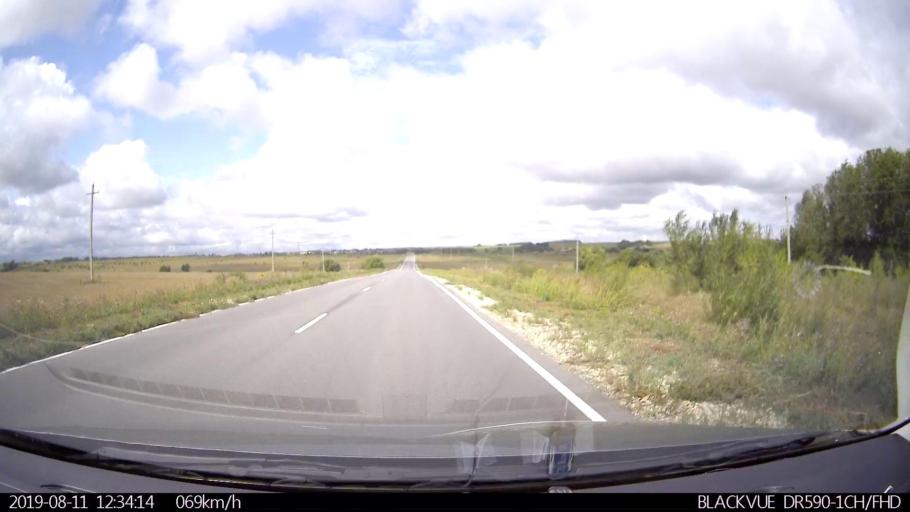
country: RU
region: Ulyanovsk
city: Ignatovka
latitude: 53.8154
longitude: 47.8450
